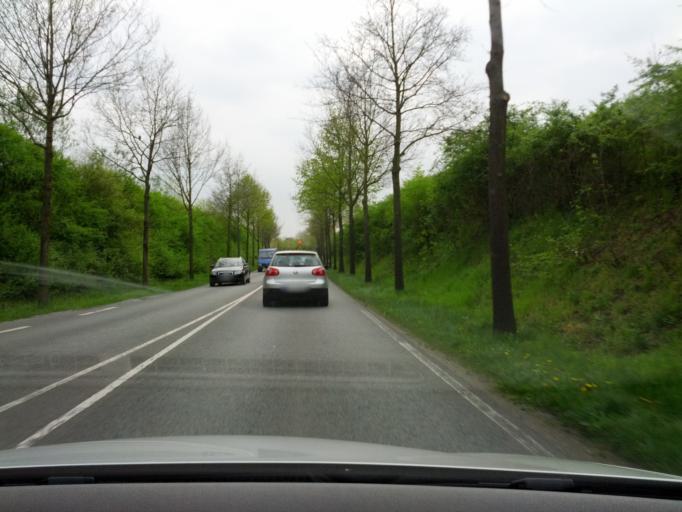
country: DE
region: North Rhine-Westphalia
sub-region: Regierungsbezirk Detmold
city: Guetersloh
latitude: 51.8879
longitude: 8.3928
